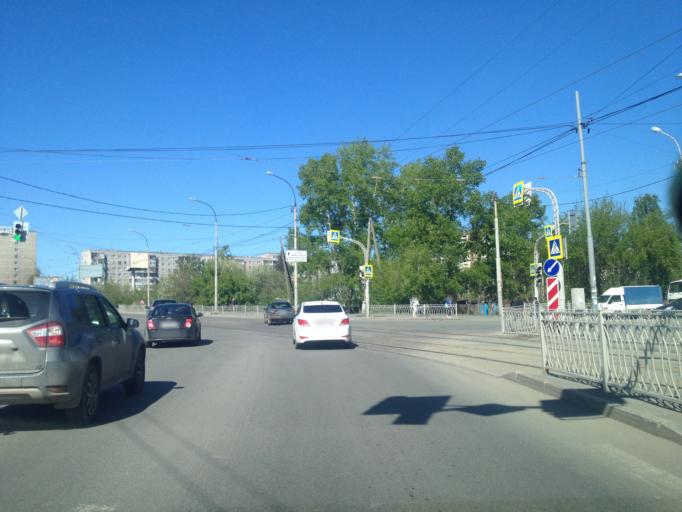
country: RU
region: Sverdlovsk
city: Sovkhoznyy
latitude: 56.8241
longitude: 60.5429
